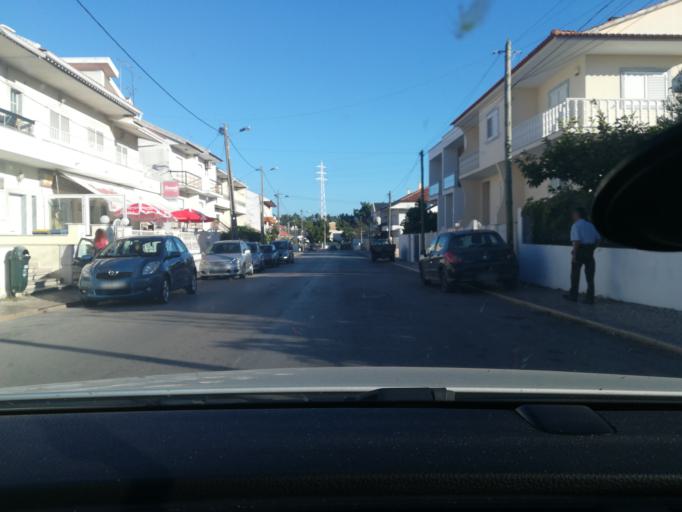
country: PT
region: Setubal
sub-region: Seixal
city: Corroios
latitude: 38.6321
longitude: -9.1586
